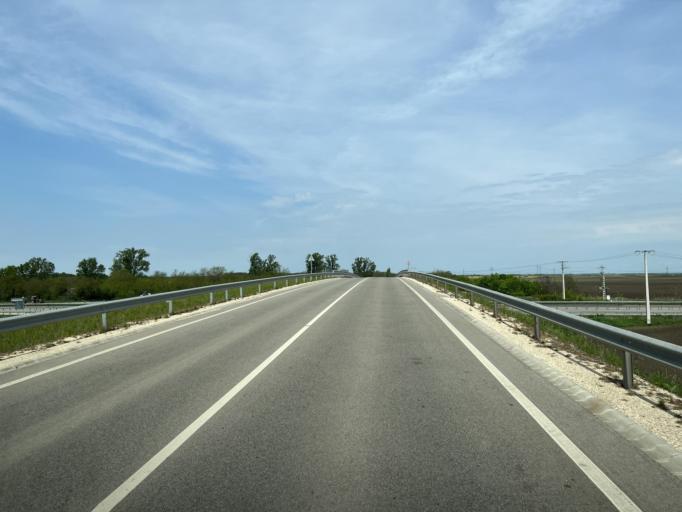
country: HU
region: Pest
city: Abony
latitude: 47.2157
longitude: 19.9803
